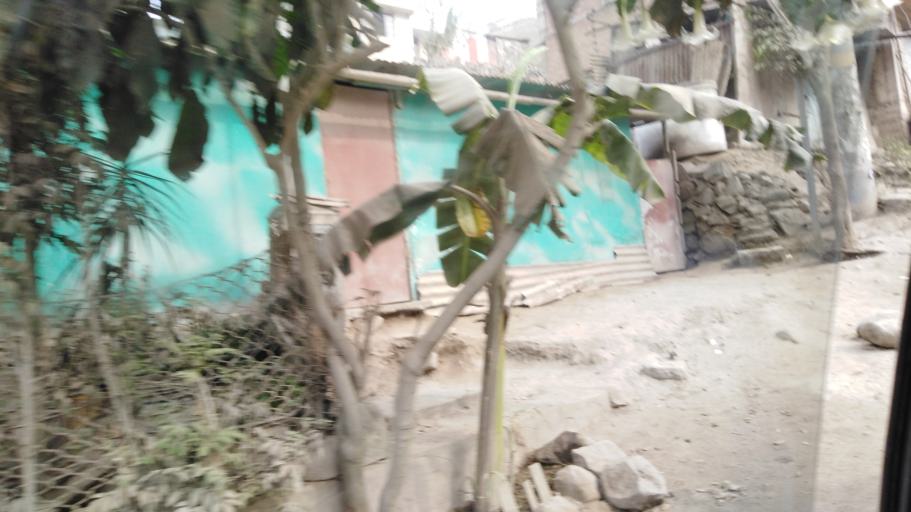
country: PE
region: Lima
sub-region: Lima
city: La Molina
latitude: -12.1463
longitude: -76.9271
